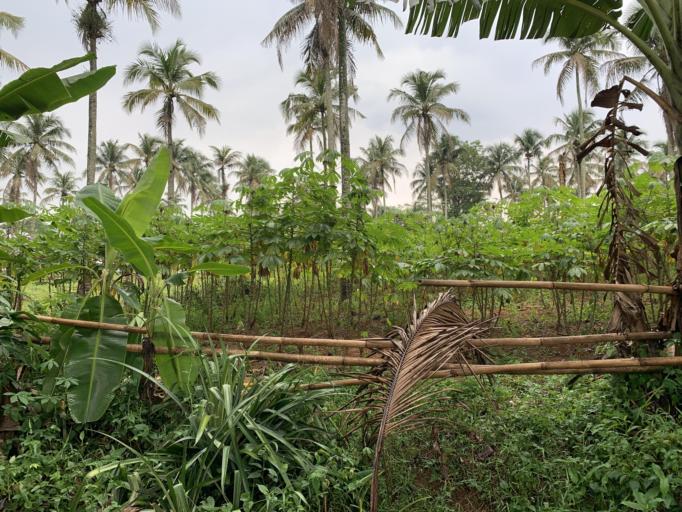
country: ID
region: West Java
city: Parung
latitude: -6.4191
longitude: 106.6291
